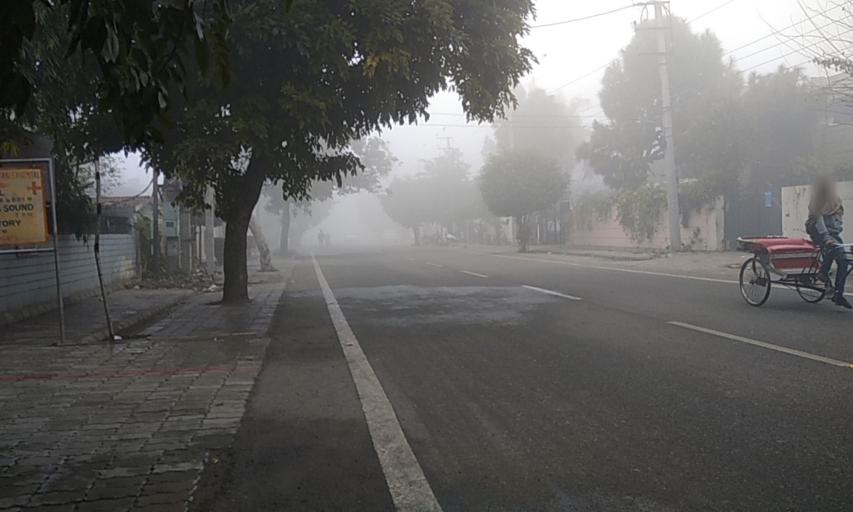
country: IN
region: Punjab
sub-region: Amritsar
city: Amritsar
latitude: 31.6452
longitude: 74.8667
